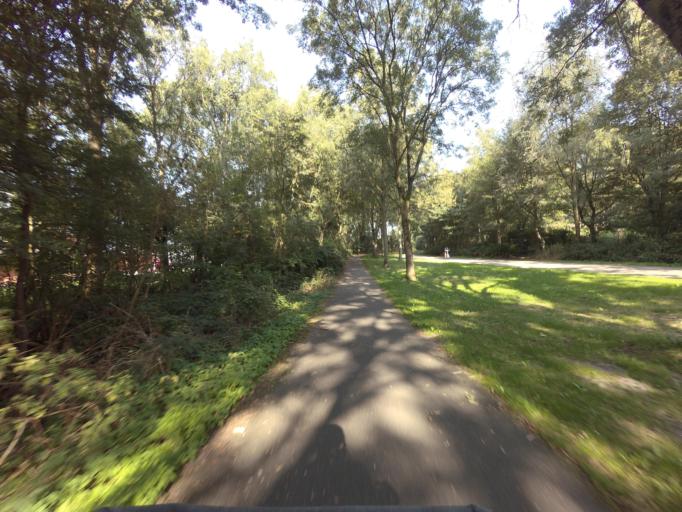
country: NL
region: Groningen
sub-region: Gemeente Groningen
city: Groningen
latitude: 53.1756
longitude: 6.5463
